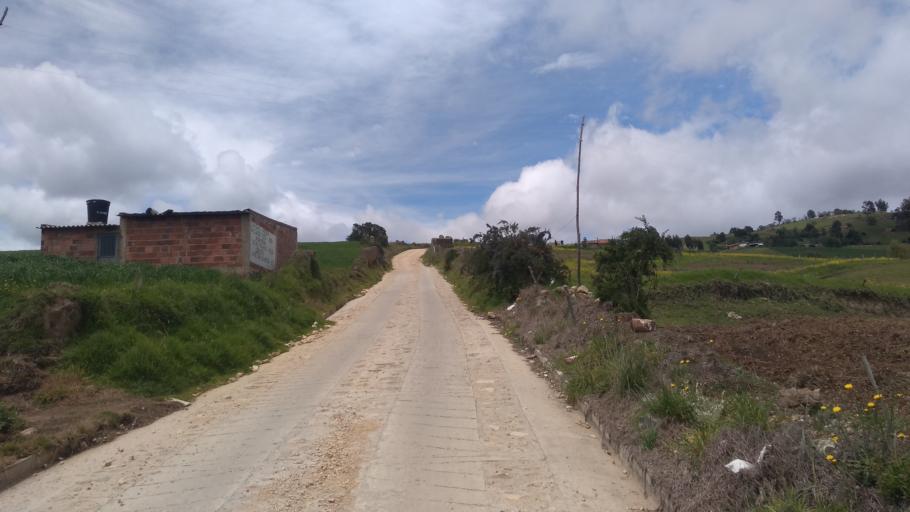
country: CO
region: Boyaca
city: Toca
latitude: 5.5619
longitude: -73.1770
